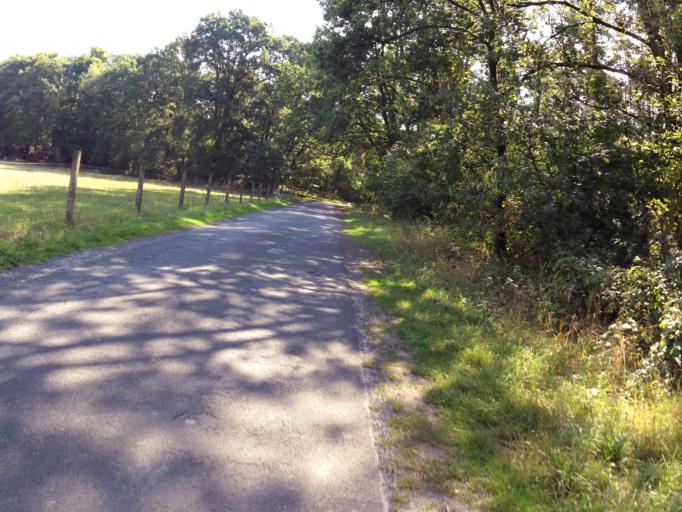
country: DE
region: North Rhine-Westphalia
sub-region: Regierungsbezirk Detmold
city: Harsewinkel
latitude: 51.9513
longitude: 8.2329
